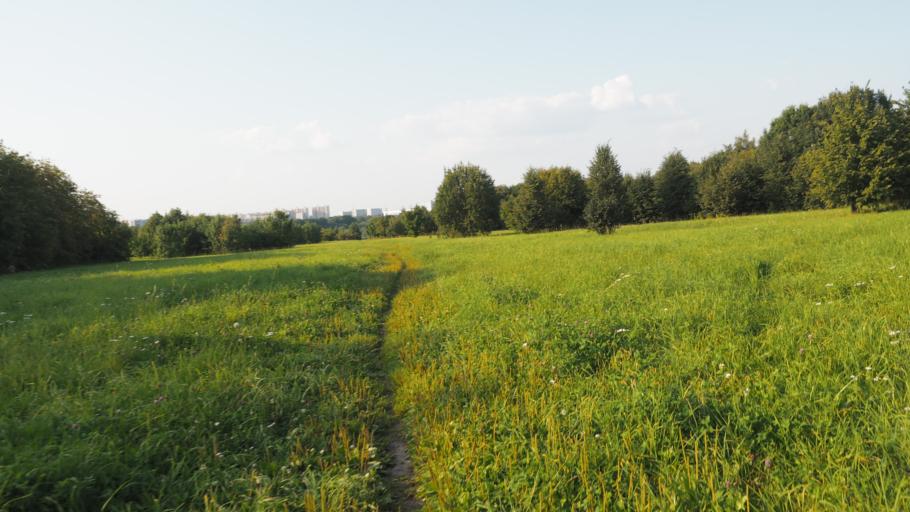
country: RU
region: Moscow
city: Orekhovo-Borisovo Severnoye
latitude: 55.6223
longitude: 37.6900
